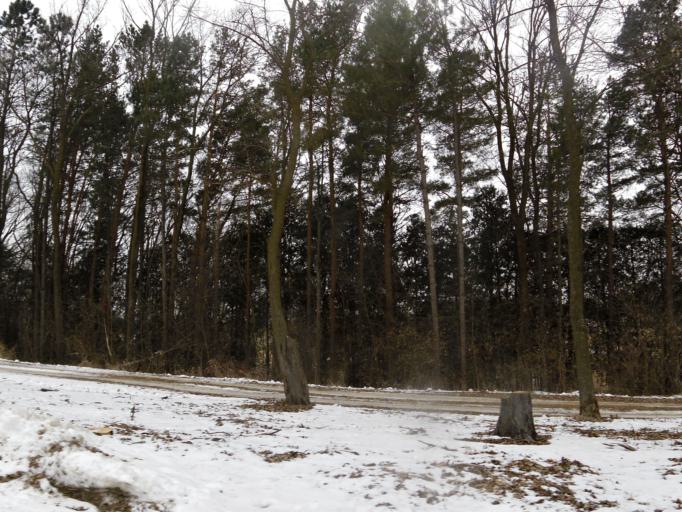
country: US
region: Minnesota
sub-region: Carver County
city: Watertown
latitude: 45.0138
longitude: -93.8519
